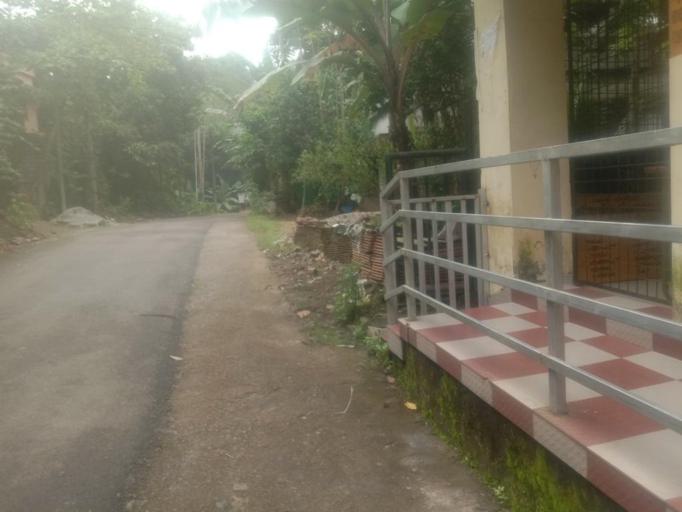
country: IN
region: Kerala
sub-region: Thiruvananthapuram
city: Nedumangad
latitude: 8.6986
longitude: 76.9572
